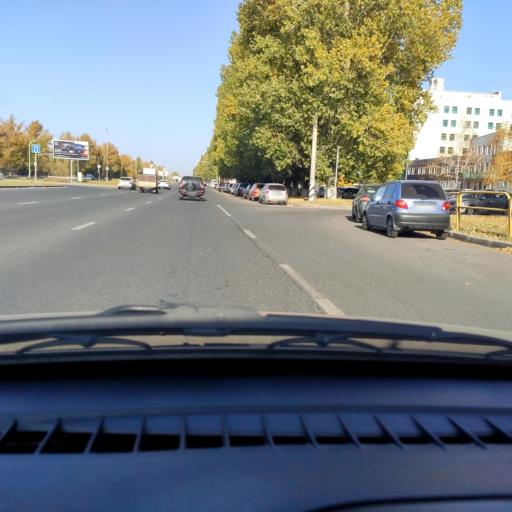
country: RU
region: Samara
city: Tol'yatti
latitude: 53.5075
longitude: 49.2767
